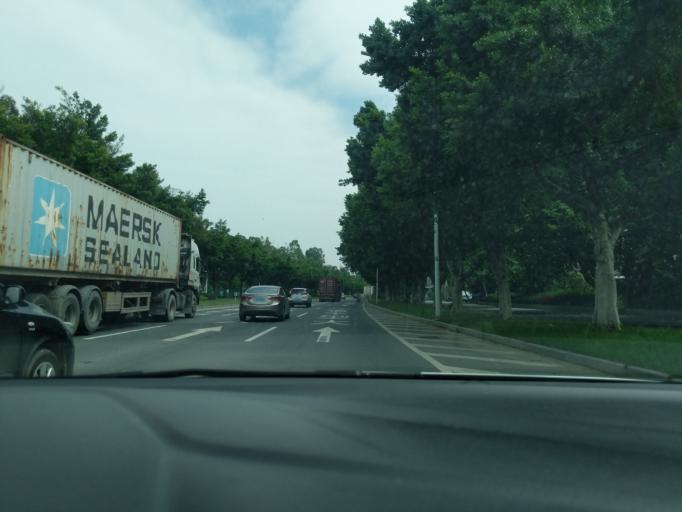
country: CN
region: Guangdong
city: Nansha
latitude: 22.7545
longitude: 113.5743
